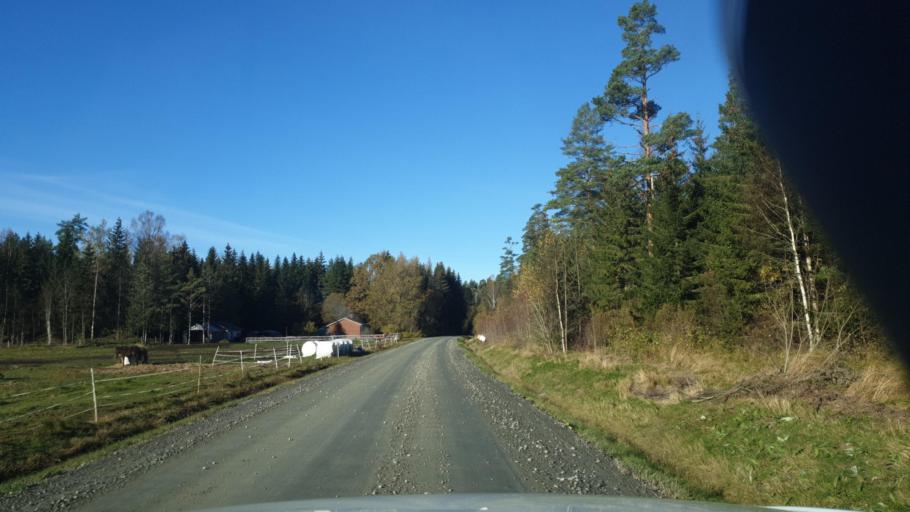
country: SE
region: Vaermland
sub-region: Karlstads Kommun
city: Edsvalla
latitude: 59.4499
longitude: 13.1519
